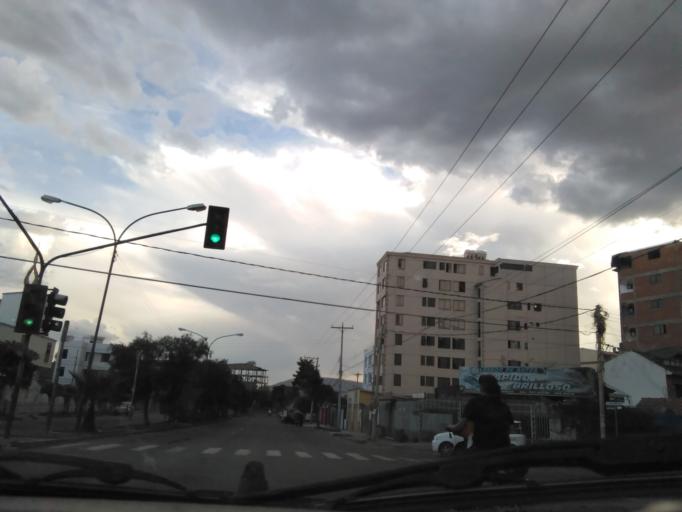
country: BO
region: Cochabamba
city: Cochabamba
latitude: -17.3820
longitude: -66.1766
